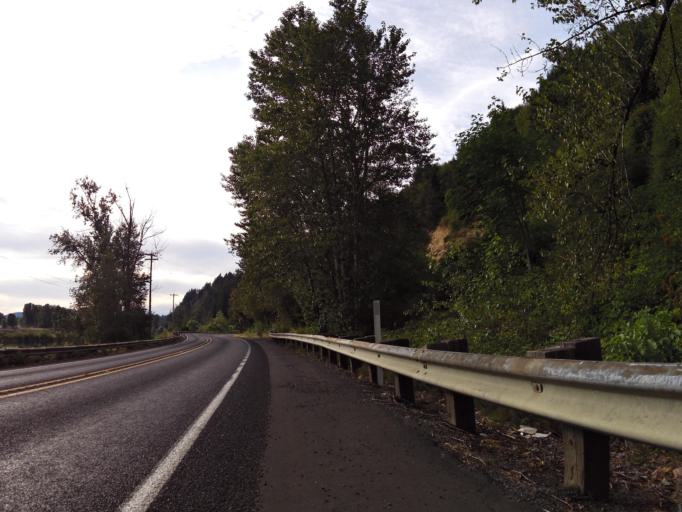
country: US
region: Washington
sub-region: Cowlitz County
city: West Longview
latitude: 46.1872
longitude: -123.0871
